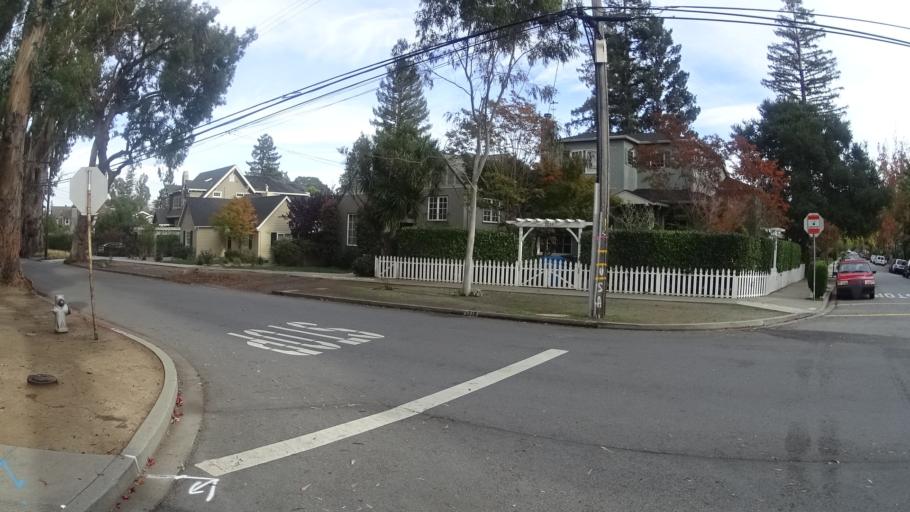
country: US
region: California
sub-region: San Mateo County
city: Burlingame
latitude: 37.5840
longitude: -122.3712
